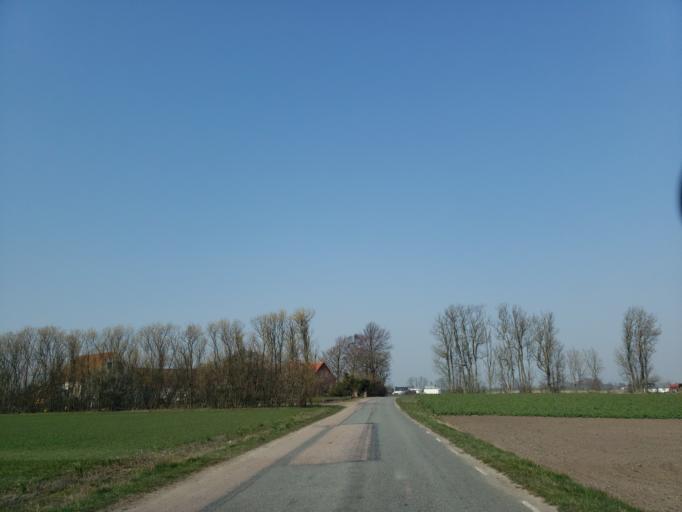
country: SE
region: Skane
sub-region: Simrishamns Kommun
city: Simrishamn
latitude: 55.4638
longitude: 14.2088
